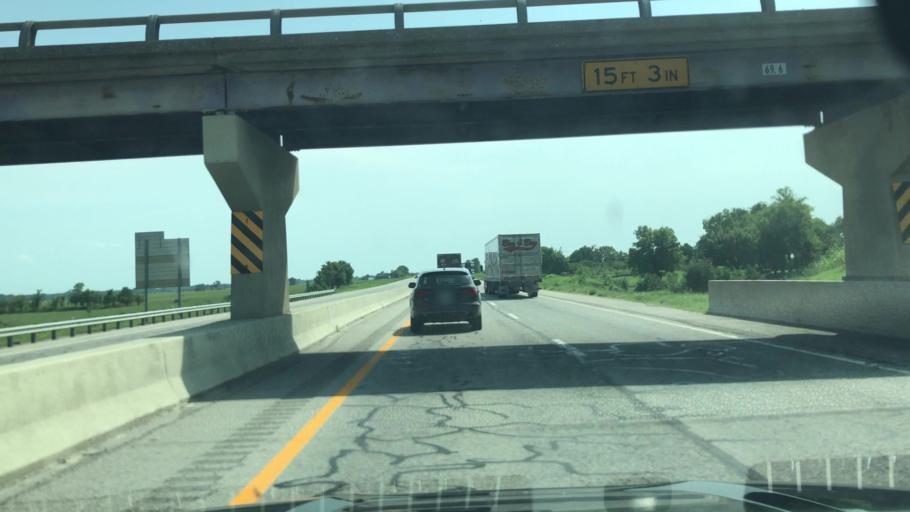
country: US
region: Oklahoma
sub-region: Ottawa County
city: Miami
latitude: 36.8302
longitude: -94.8667
